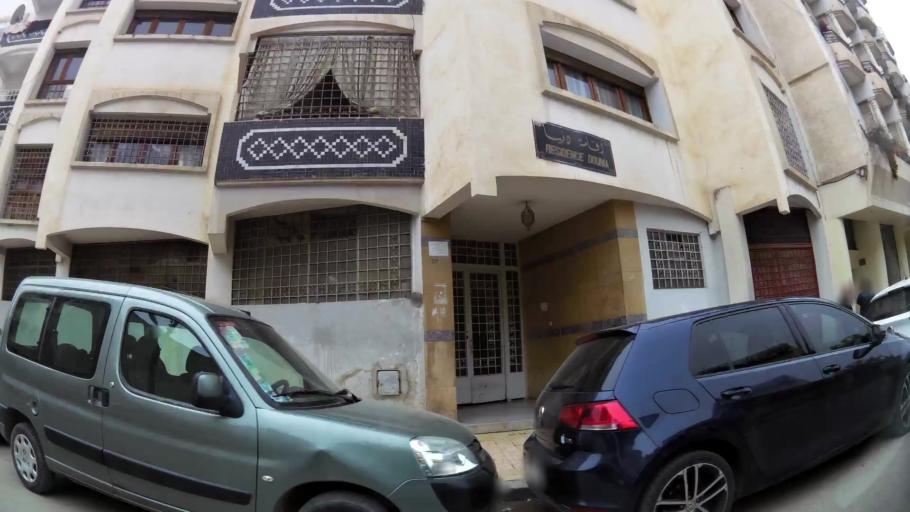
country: MA
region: Fes-Boulemane
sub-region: Fes
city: Fes
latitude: 34.0345
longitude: -4.9955
